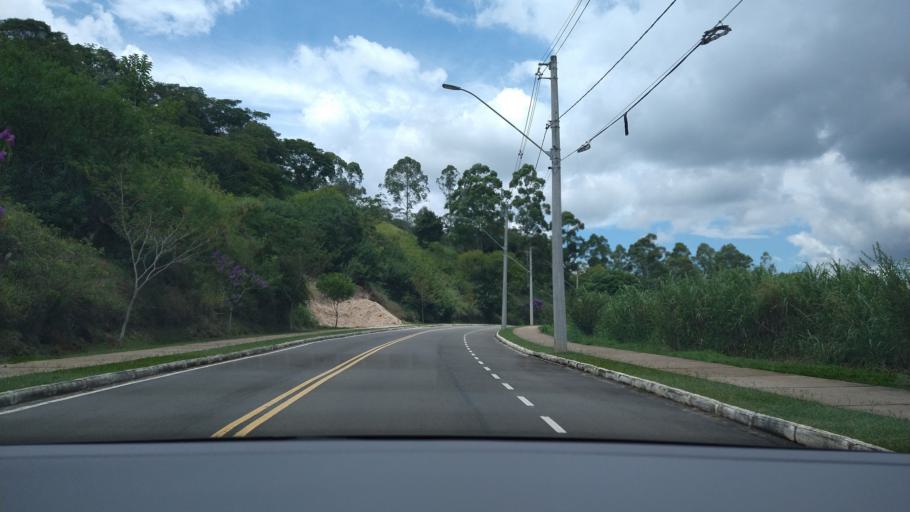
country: BR
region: Minas Gerais
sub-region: Vicosa
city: Vicosa
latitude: -20.7628
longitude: -42.8586
